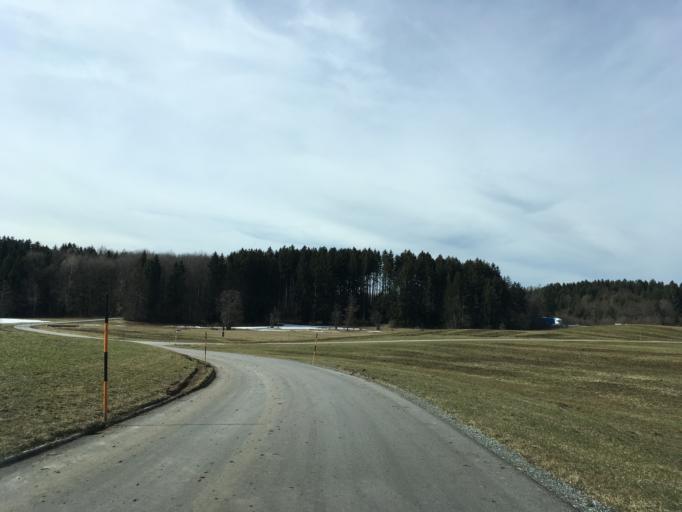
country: DE
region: Bavaria
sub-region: Upper Bavaria
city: Aschau im Chiemgau
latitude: 47.8045
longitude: 12.3353
